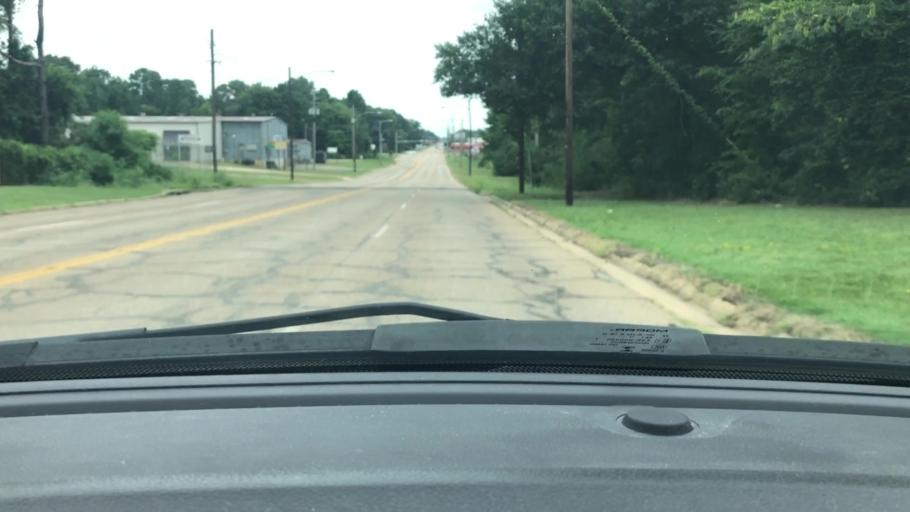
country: US
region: Texas
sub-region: Bowie County
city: Wake Village
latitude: 33.4172
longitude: -94.0803
